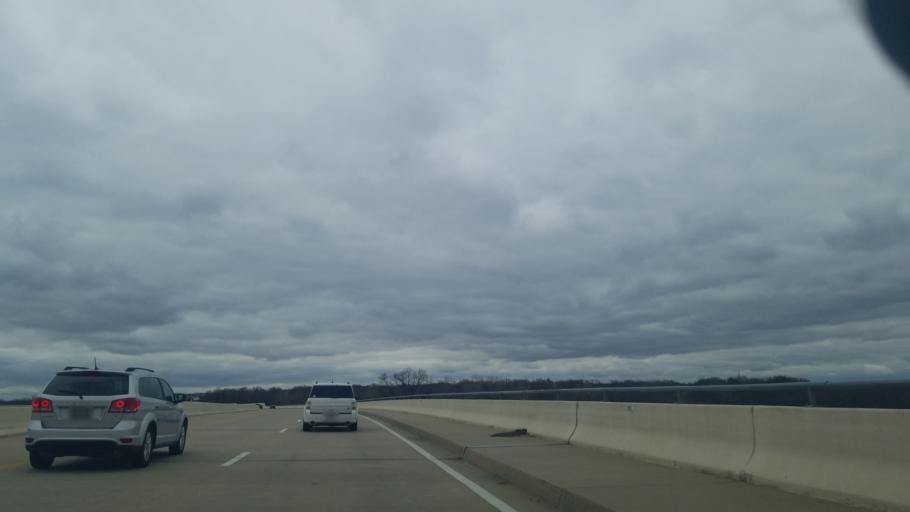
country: US
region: Texas
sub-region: Denton County
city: Copper Canyon
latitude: 33.1212
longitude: -97.0814
